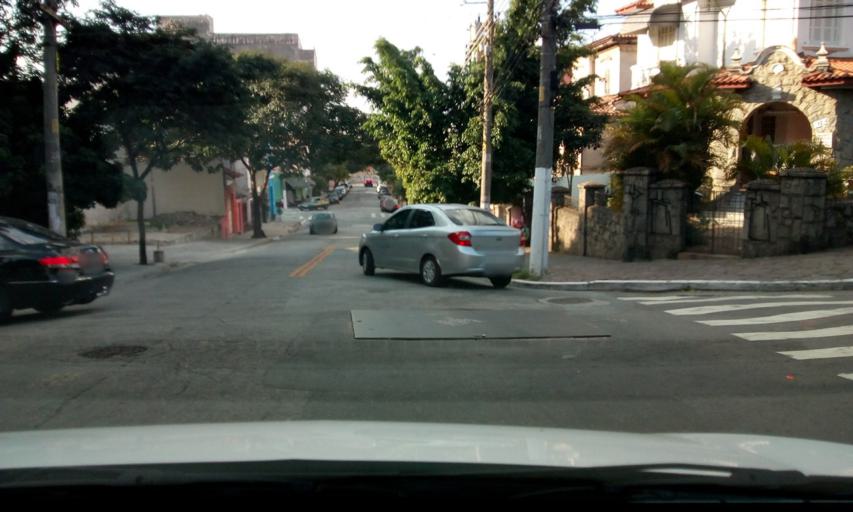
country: BR
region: Sao Paulo
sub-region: Sao Paulo
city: Sao Paulo
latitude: -23.5632
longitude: -46.6266
